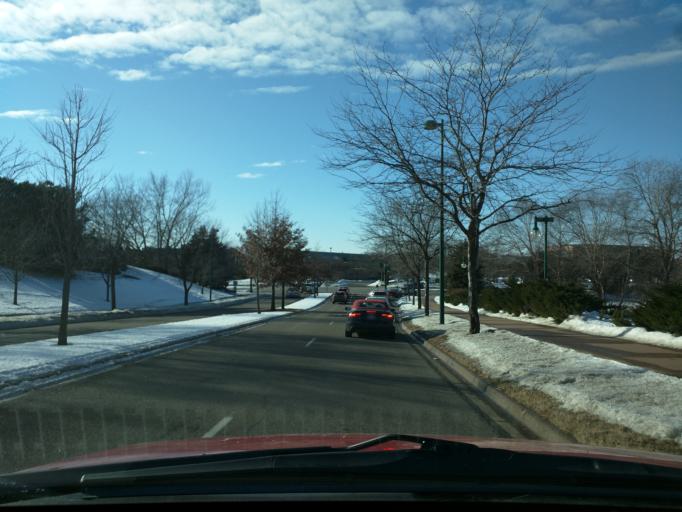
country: US
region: Minnesota
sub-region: Hennepin County
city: Eden Prairie
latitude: 44.8572
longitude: -93.4340
